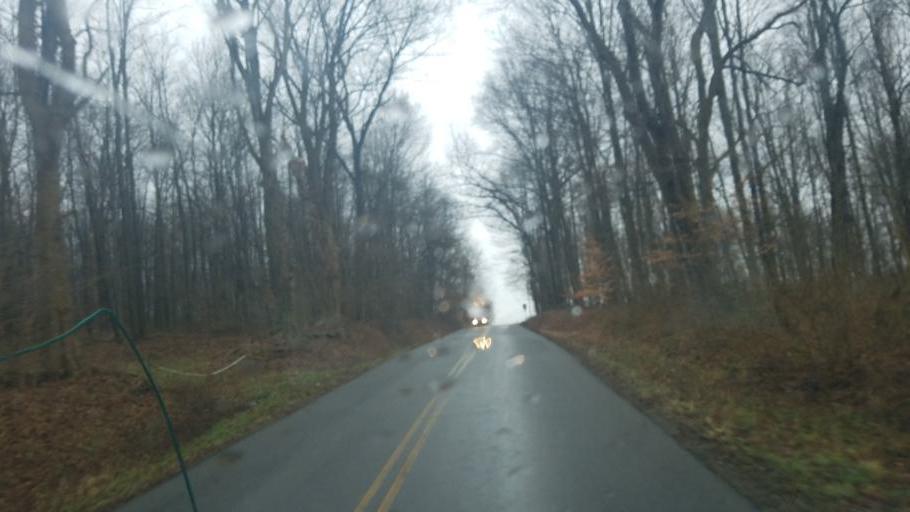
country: US
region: Ohio
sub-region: Knox County
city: Fredericktown
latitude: 40.4695
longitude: -82.4839
